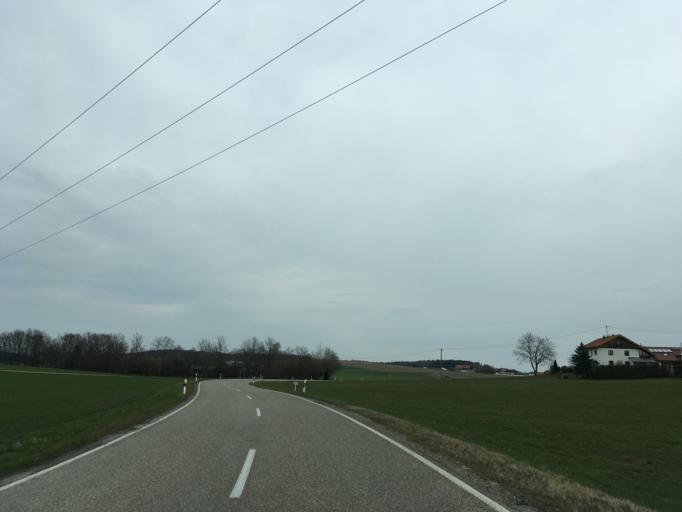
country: DE
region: Bavaria
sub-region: Upper Bavaria
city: Schnaitsee
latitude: 48.0440
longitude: 12.3726
